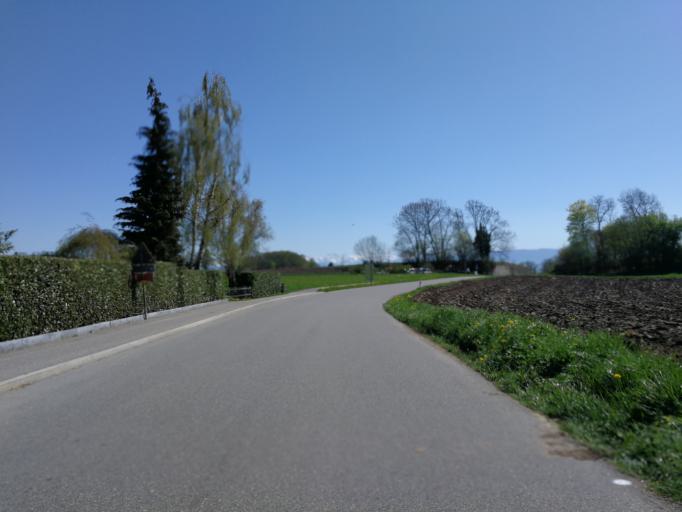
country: CH
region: Zurich
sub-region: Bezirk Meilen
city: Herrliberg
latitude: 47.2939
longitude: 8.6311
